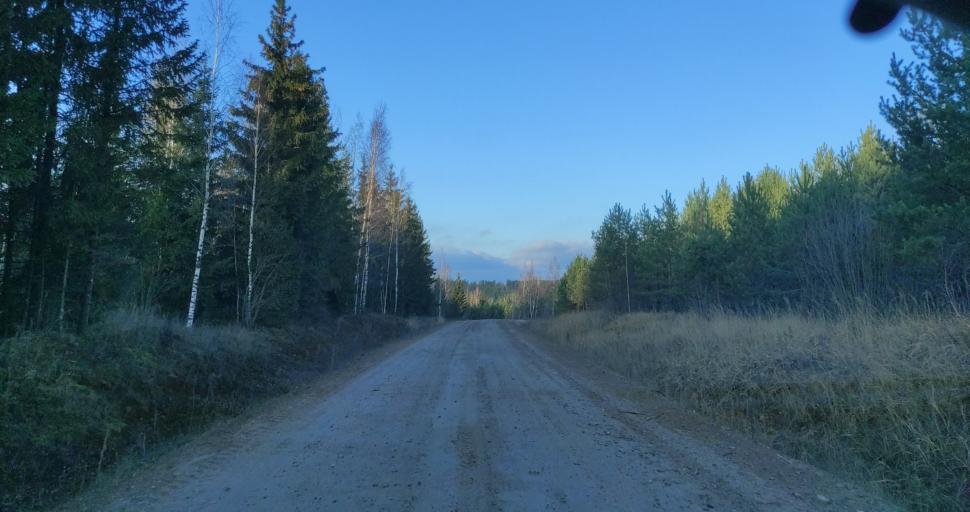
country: LV
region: Kuldigas Rajons
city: Kuldiga
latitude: 57.0565
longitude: 21.8662
